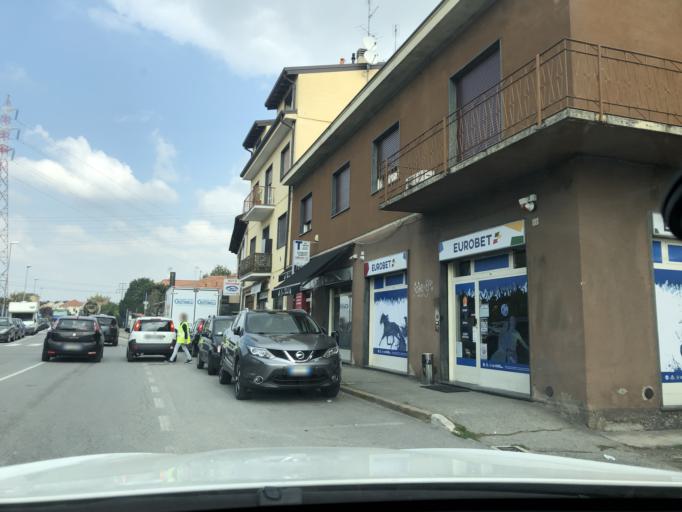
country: IT
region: Lombardy
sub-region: Provincia di Monza e Brianza
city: Brugherio
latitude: 45.5431
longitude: 9.3038
